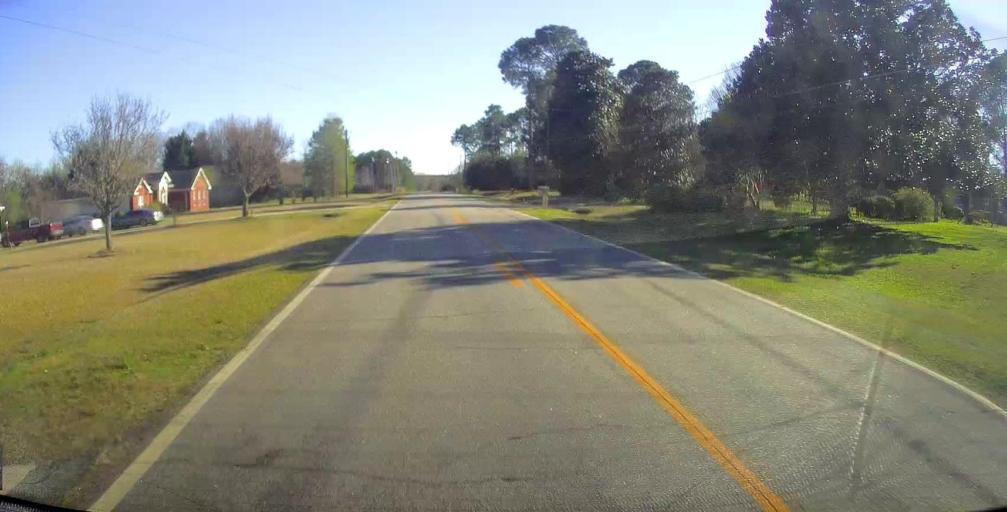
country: US
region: Georgia
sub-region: Peach County
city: Fort Valley
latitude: 32.5639
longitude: -83.9160
